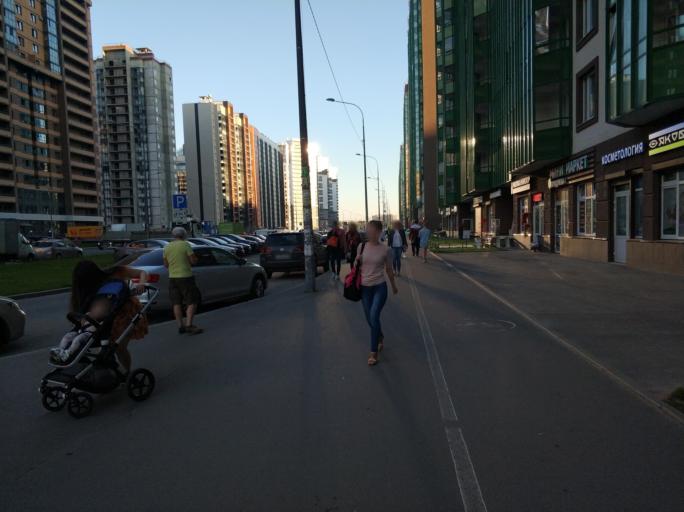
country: RU
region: Leningrad
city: Murino
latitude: 60.0571
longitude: 30.4281
